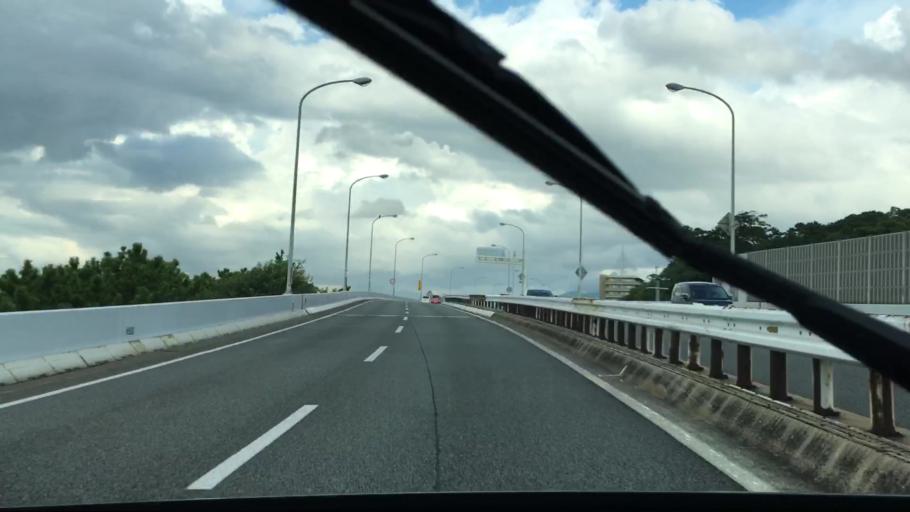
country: JP
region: Fukuoka
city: Fukuoka-shi
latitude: 33.6000
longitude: 130.3716
